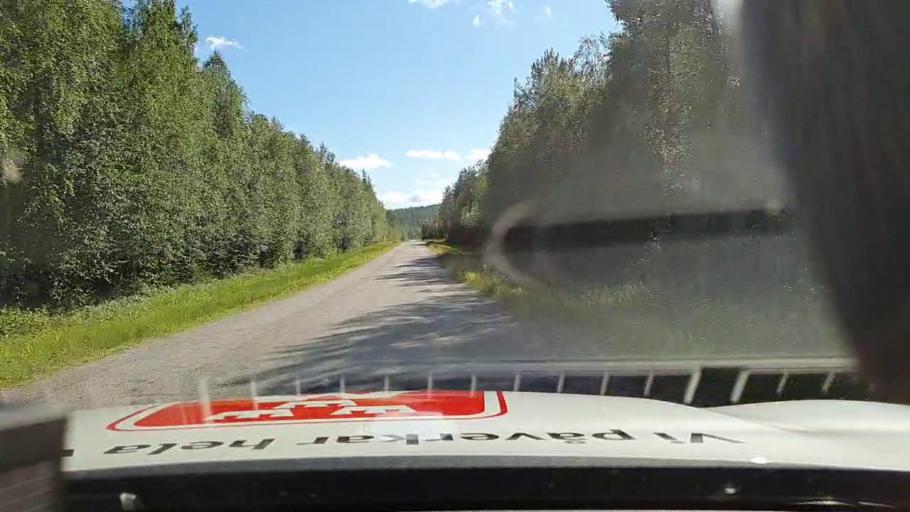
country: SE
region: Norrbotten
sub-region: Overkalix Kommun
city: OEverkalix
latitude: 66.2508
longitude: 23.0117
